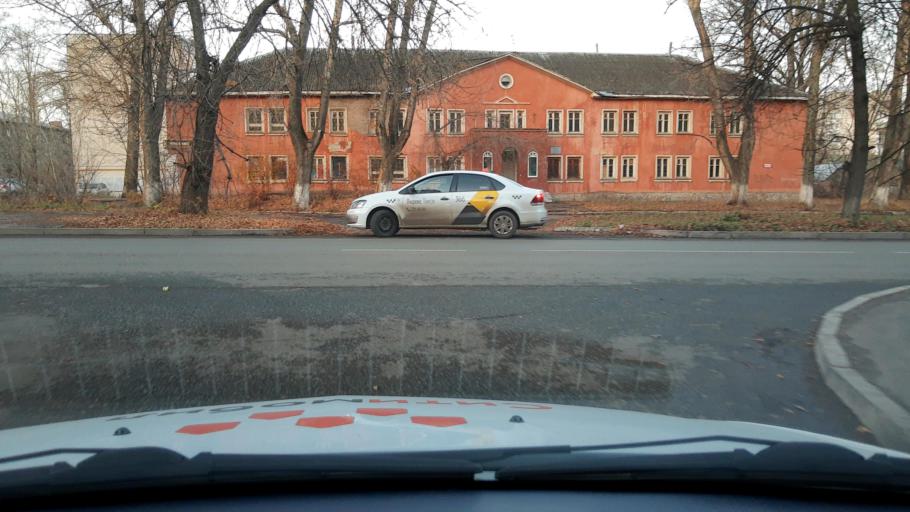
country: RU
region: Bashkortostan
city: Ufa
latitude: 54.8158
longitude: 56.1166
